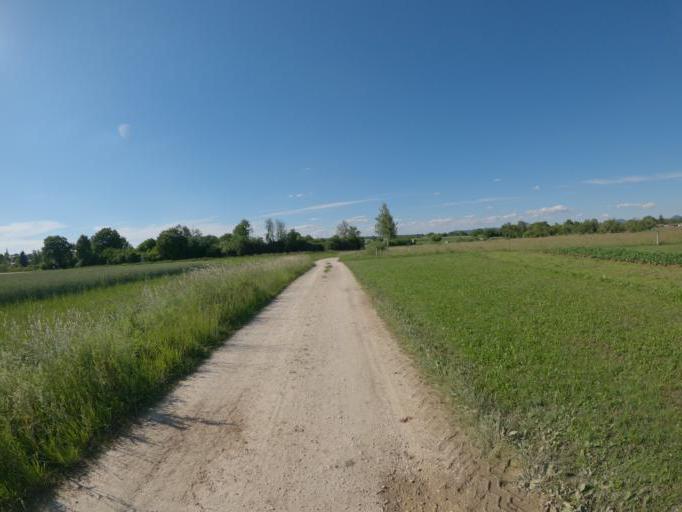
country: DE
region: Baden-Wuerttemberg
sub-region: Regierungsbezirk Stuttgart
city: Heiningen
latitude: 48.6575
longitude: 9.6597
